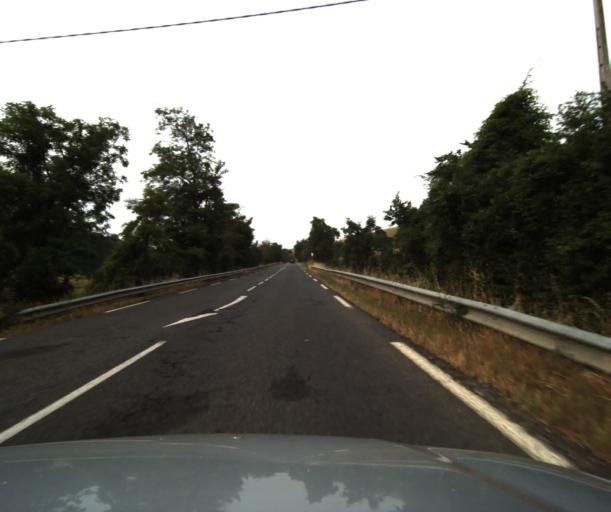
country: FR
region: Midi-Pyrenees
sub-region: Departement du Gers
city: Mirande
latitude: 43.5592
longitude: 0.4986
